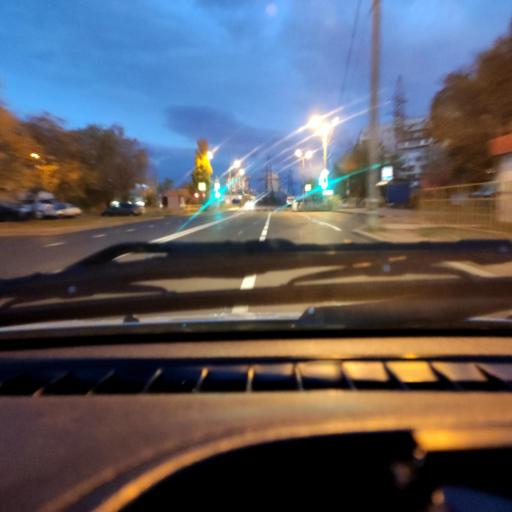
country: RU
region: Samara
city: Zhigulevsk
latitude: 53.4714
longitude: 49.5328
